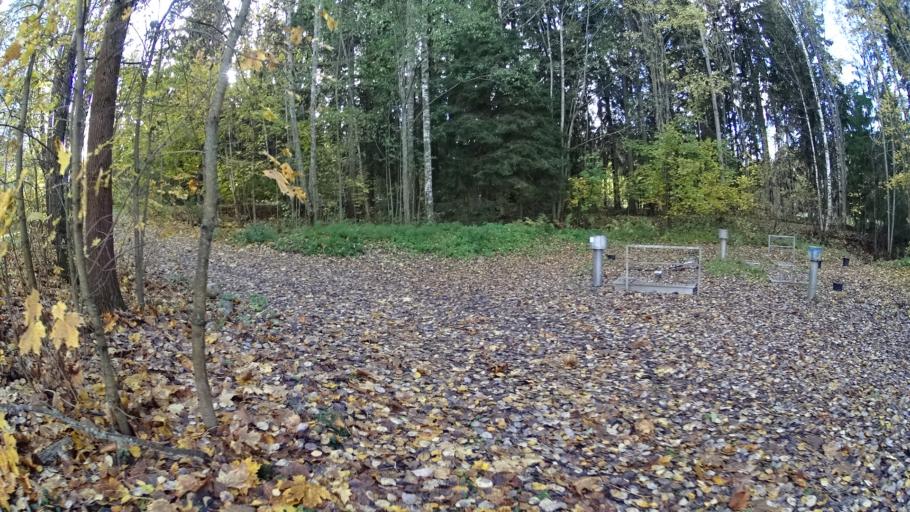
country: FI
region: Uusimaa
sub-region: Helsinki
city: Kilo
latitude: 60.2810
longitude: 24.8380
